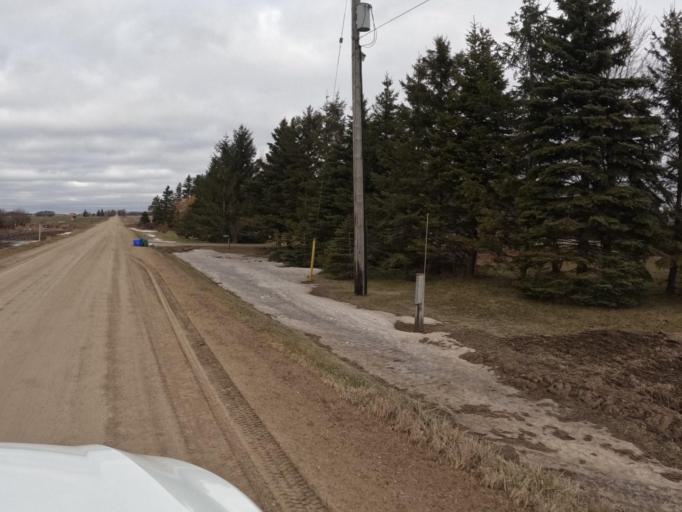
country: CA
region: Ontario
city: Shelburne
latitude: 43.8670
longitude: -80.4011
